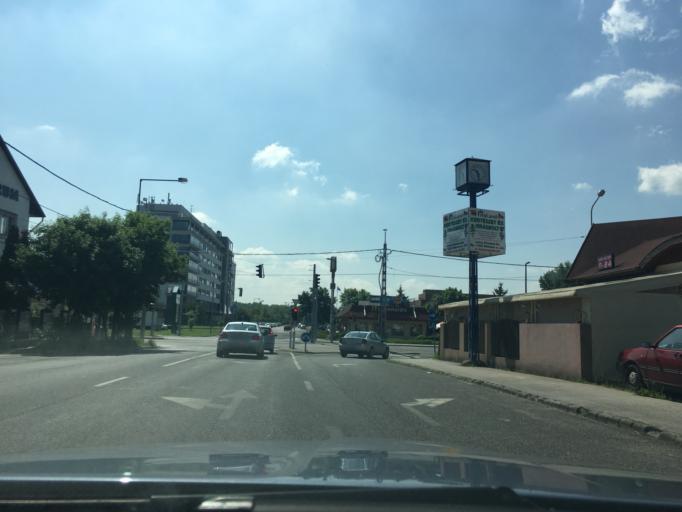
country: HU
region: Budapest
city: Budapest XXII. keruelet
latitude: 47.4107
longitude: 19.0205
